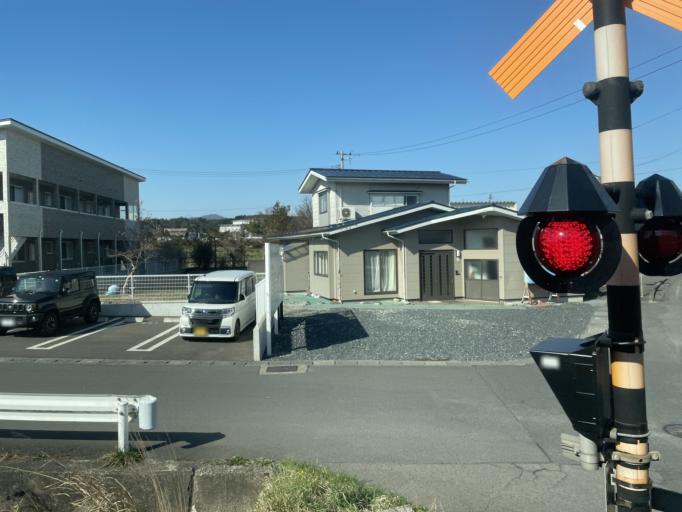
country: JP
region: Aomori
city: Hachinohe
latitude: 40.4124
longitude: 141.7145
